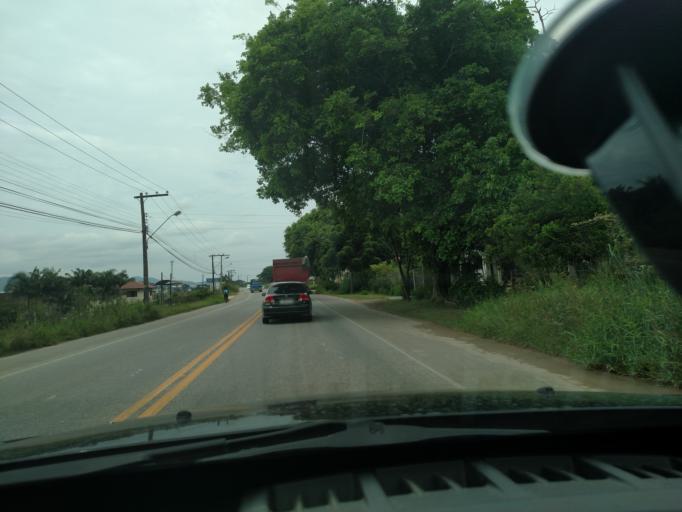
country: BR
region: Santa Catarina
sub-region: Itajai
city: Itajai
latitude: -26.8876
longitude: -48.7526
